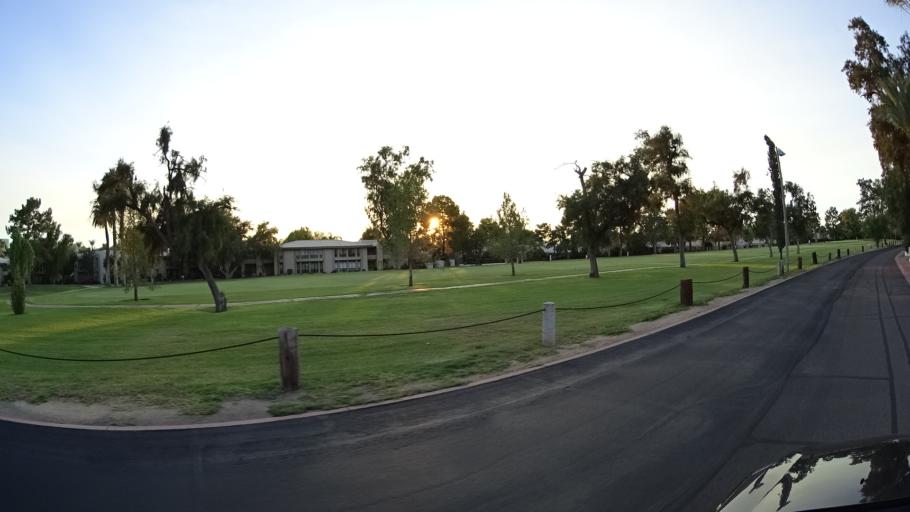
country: US
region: Arizona
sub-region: Maricopa County
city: Phoenix
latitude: 33.5133
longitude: -112.0248
